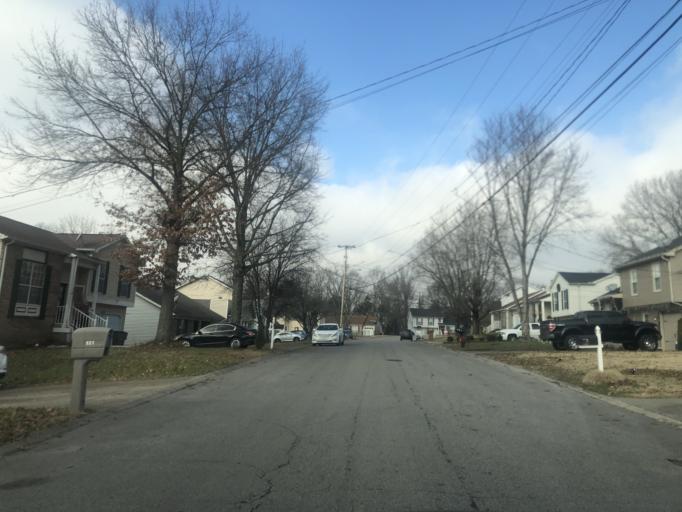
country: US
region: Tennessee
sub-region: Rutherford County
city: La Vergne
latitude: 36.0810
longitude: -86.6595
